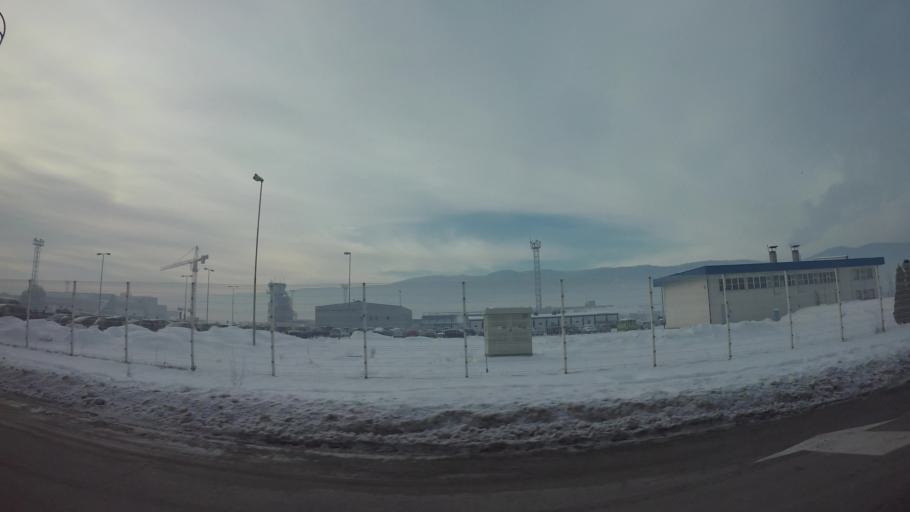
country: BA
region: Federation of Bosnia and Herzegovina
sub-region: Kanton Sarajevo
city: Sarajevo
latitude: 43.8282
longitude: 18.3357
